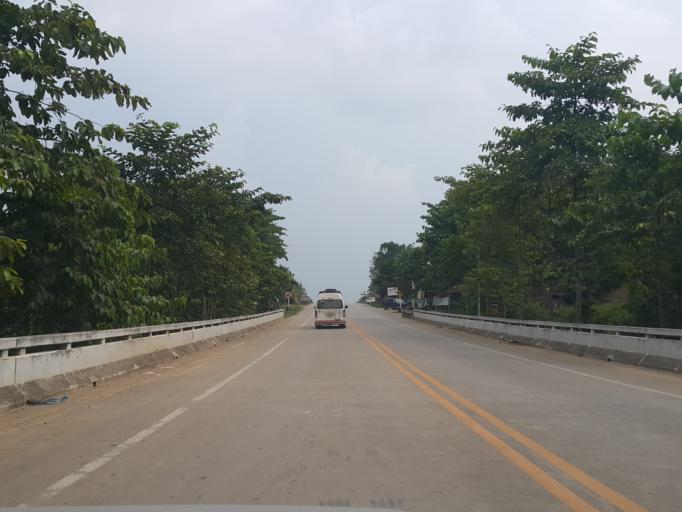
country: TH
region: Chiang Mai
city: Mae Taeng
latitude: 19.0775
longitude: 98.9236
